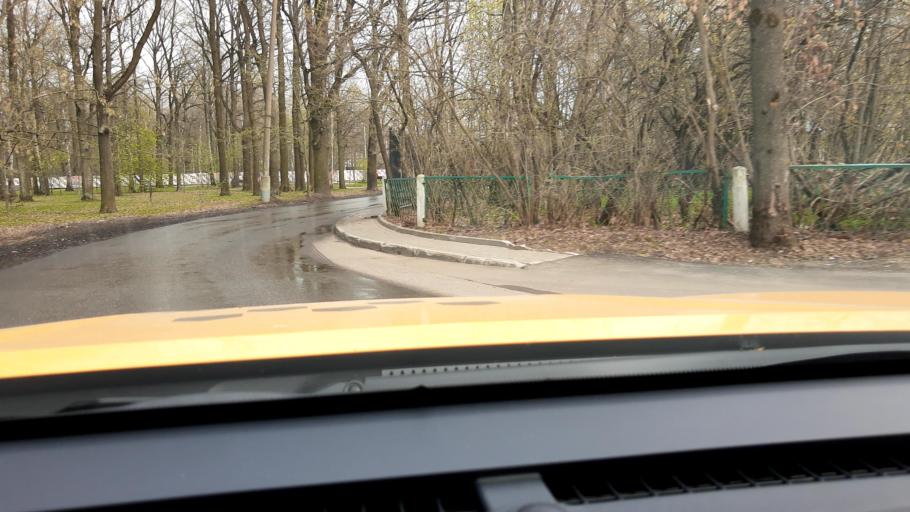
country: RU
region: Moscow
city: Severnyy
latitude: 55.9385
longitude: 37.5512
